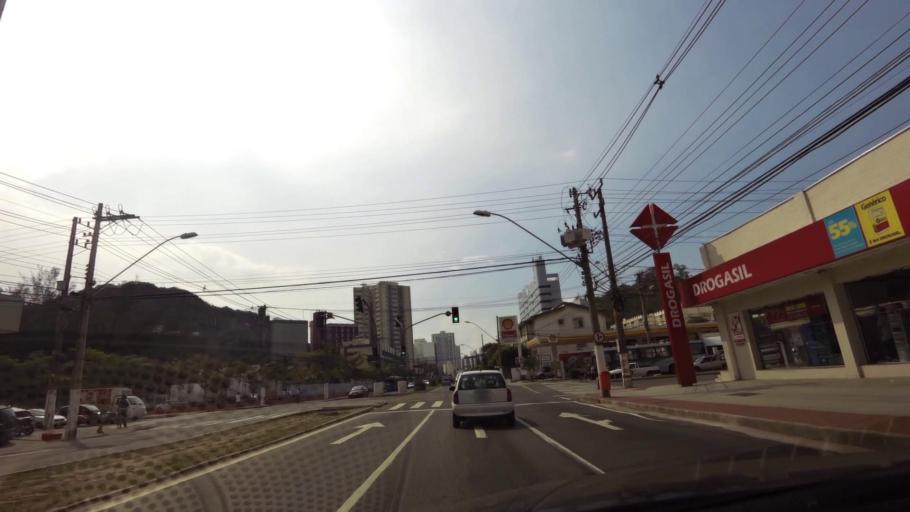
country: BR
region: Espirito Santo
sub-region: Vila Velha
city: Vila Velha
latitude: -20.3112
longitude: -40.3024
